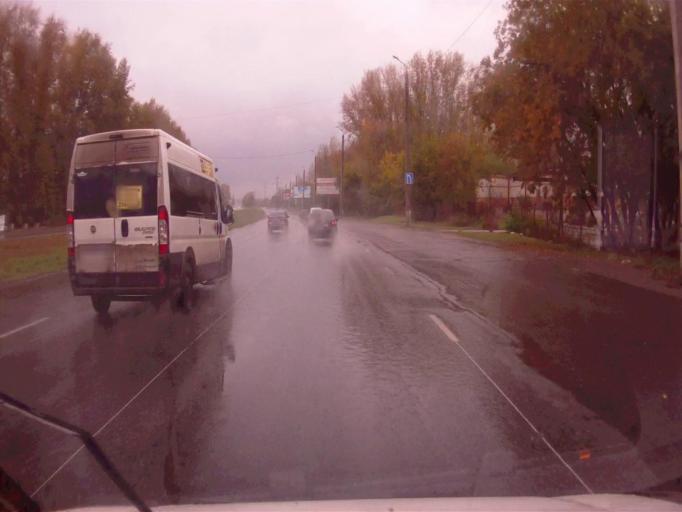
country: RU
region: Chelyabinsk
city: Dolgoderevenskoye
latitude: 55.2428
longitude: 61.3607
